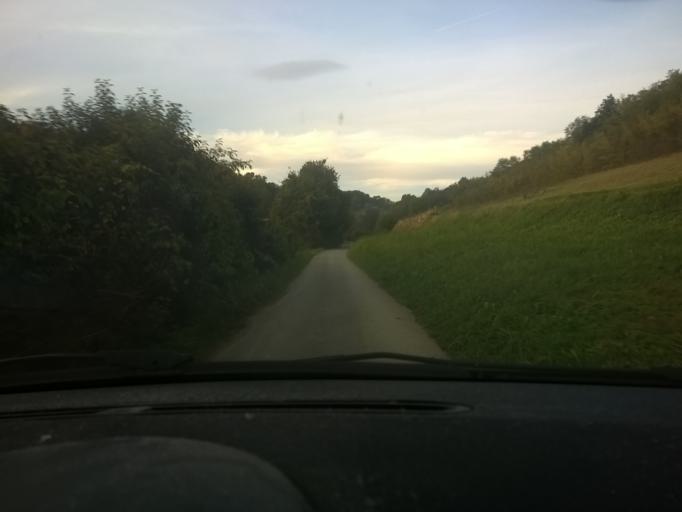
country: HR
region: Krapinsko-Zagorska
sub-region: Grad Krapina
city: Krapina
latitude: 46.1267
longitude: 15.8500
